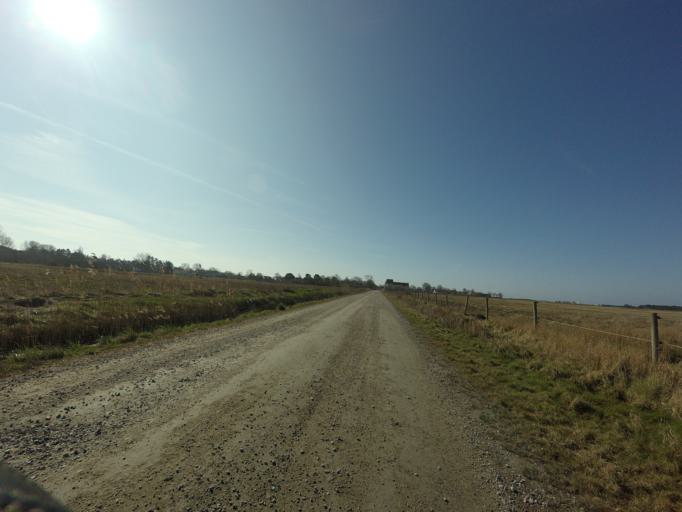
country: SE
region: Skane
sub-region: Vellinge Kommun
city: Skanor med Falsterbo
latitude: 55.4237
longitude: 12.8539
